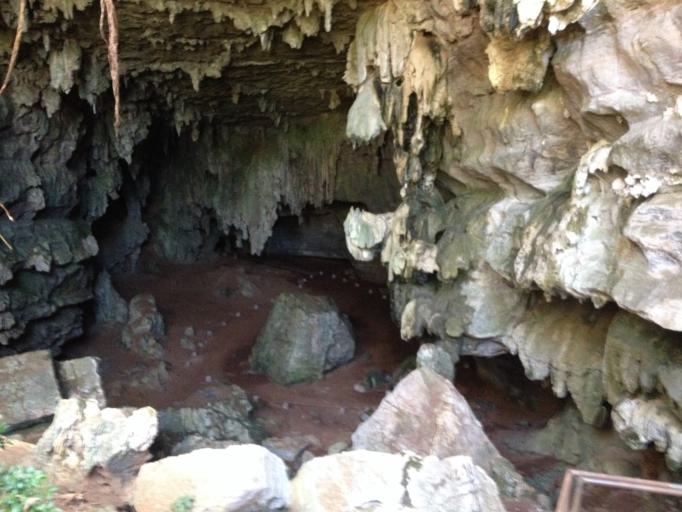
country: BR
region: Minas Gerais
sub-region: Vazante
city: Vazante
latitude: -17.9831
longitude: -46.8910
